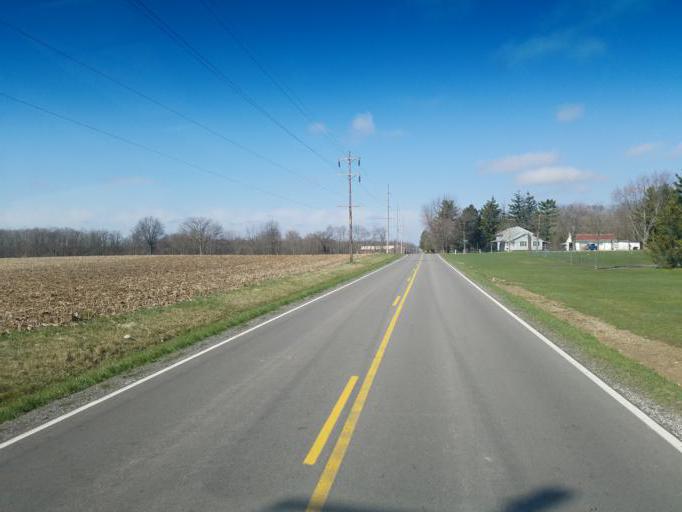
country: US
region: Ohio
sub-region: Crawford County
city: Bucyrus
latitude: 40.8338
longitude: -82.8706
